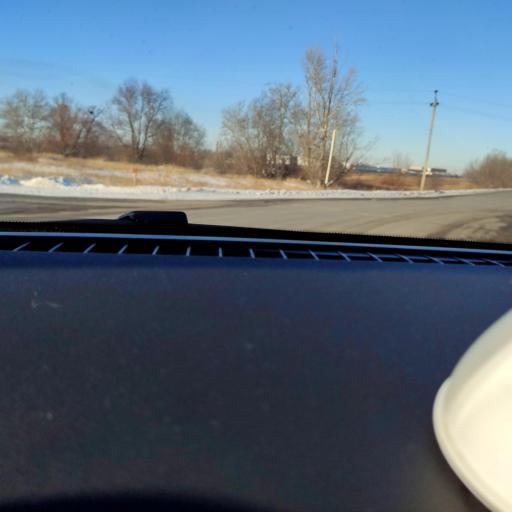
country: RU
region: Samara
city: Spiridonovka
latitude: 53.1062
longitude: 50.6421
